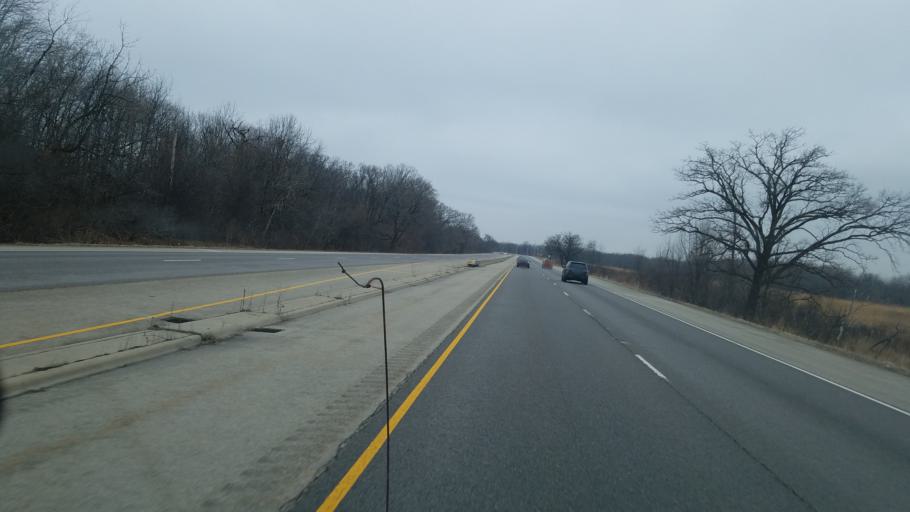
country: US
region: Illinois
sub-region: Lake County
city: Wadsworth
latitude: 42.4367
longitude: -87.9380
